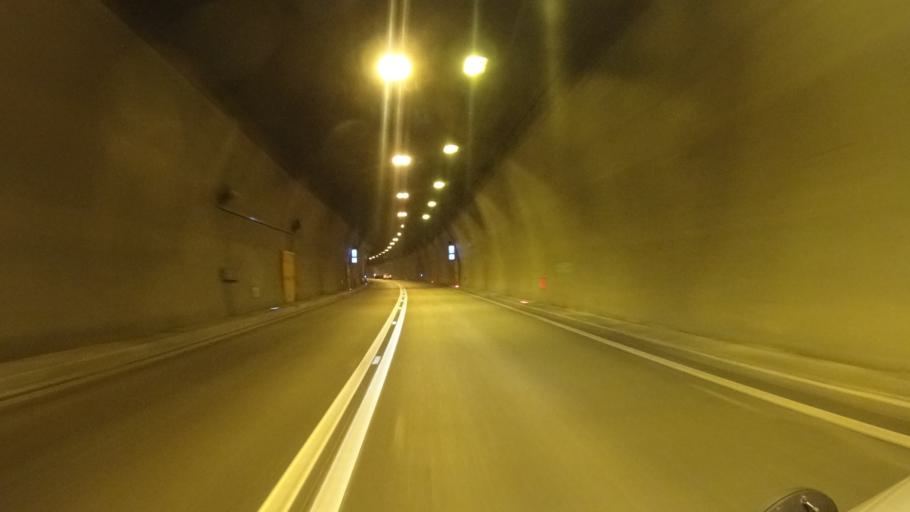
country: HR
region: Istarska
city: Lovran
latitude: 45.3123
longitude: 14.1804
